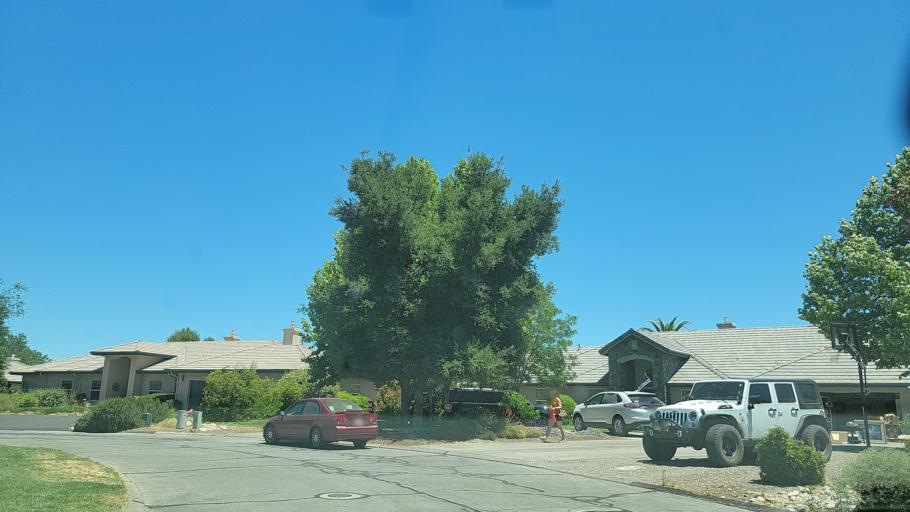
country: US
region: California
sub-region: San Luis Obispo County
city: Atascadero
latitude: 35.5102
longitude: -120.6658
